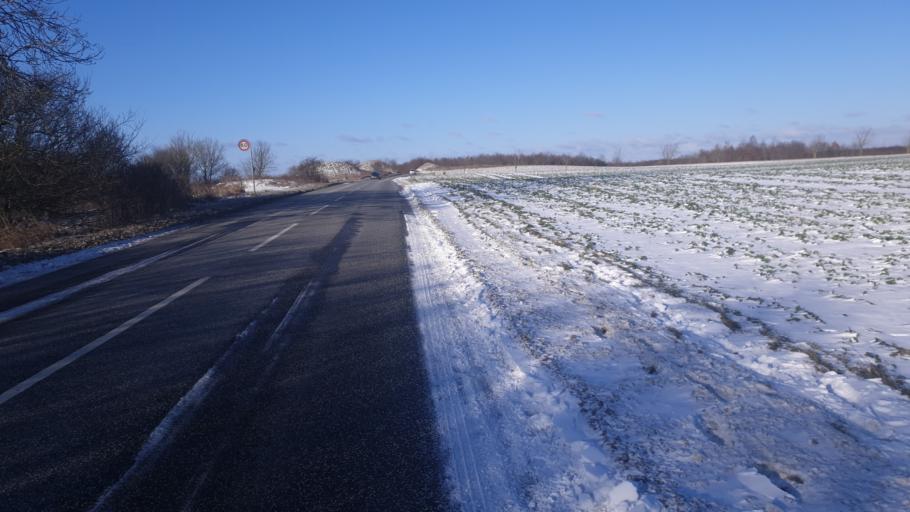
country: DK
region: Central Jutland
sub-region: Hedensted Kommune
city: Hedensted
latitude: 55.7836
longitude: 9.7104
